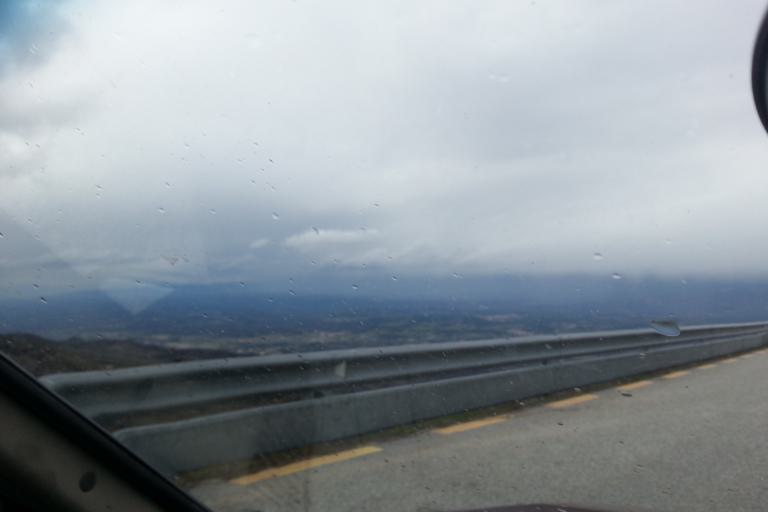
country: PT
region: Guarda
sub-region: Manteigas
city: Manteigas
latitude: 40.4363
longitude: -7.6019
